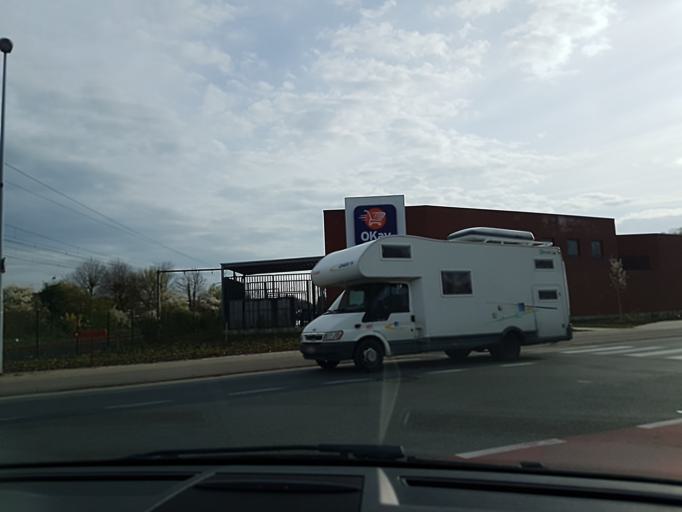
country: BE
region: Flanders
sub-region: Provincie West-Vlaanderen
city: Oostkamp
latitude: 51.1552
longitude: 3.1879
